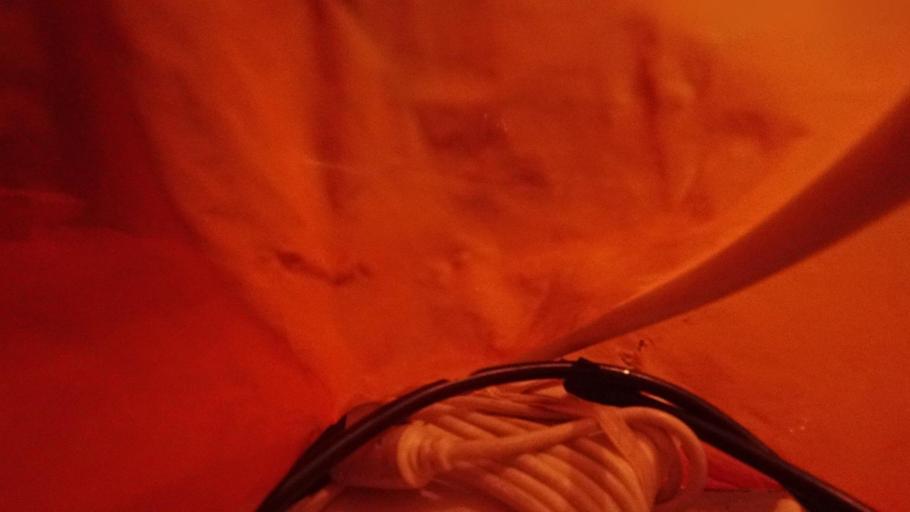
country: RU
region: Jewish Autonomous Oblast
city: Khingansk
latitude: 49.1632
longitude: 130.7685
